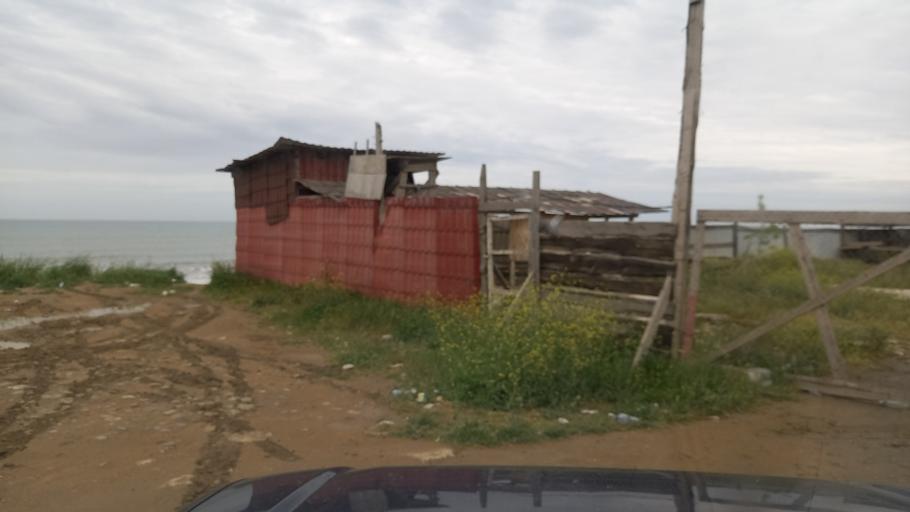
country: RU
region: Dagestan
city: Derbent
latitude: 42.0732
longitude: 48.3005
